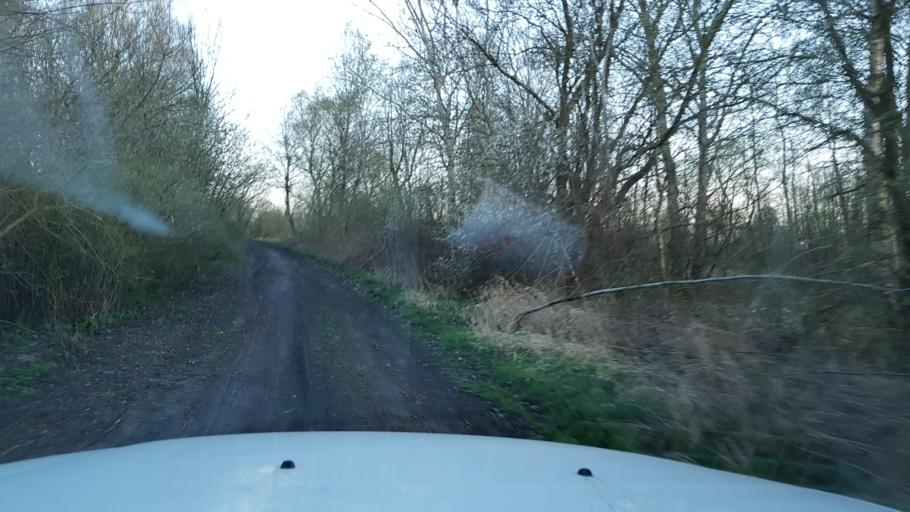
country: PL
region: West Pomeranian Voivodeship
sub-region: Powiat bialogardzki
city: Bialogard
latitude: 53.9769
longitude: 15.9563
